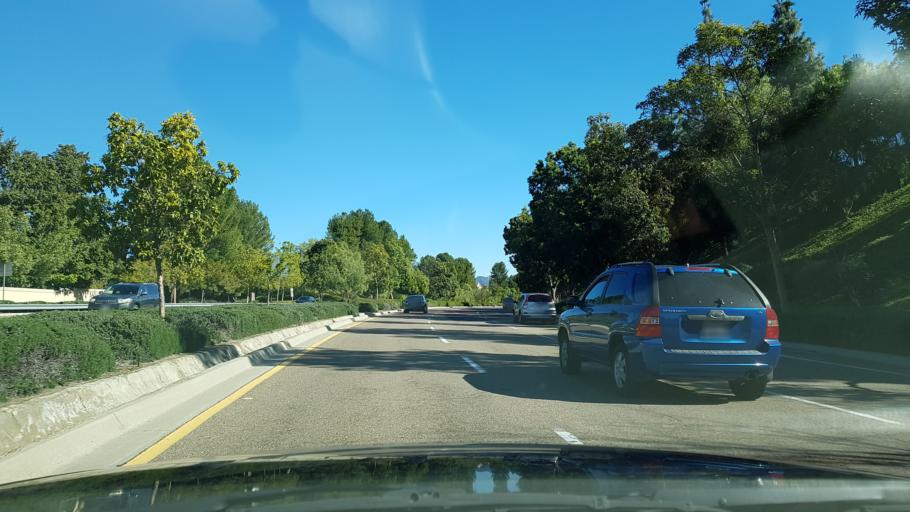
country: US
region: California
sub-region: San Diego County
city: Poway
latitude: 32.9710
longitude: -117.0791
